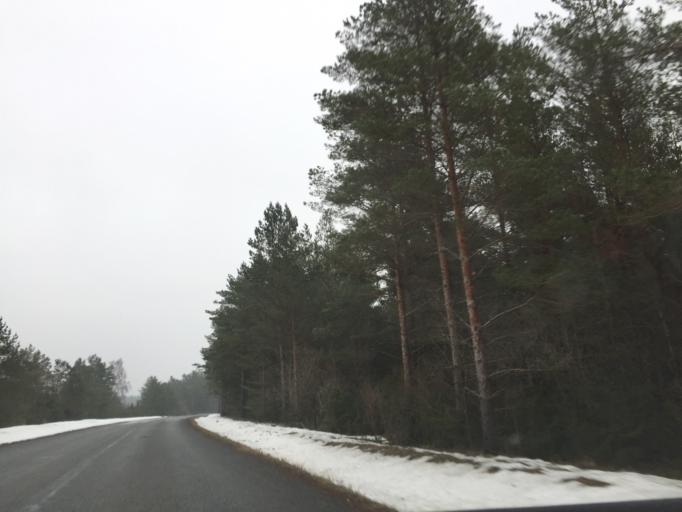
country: EE
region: Saare
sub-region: Orissaare vald
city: Orissaare
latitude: 58.4141
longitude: 22.8174
